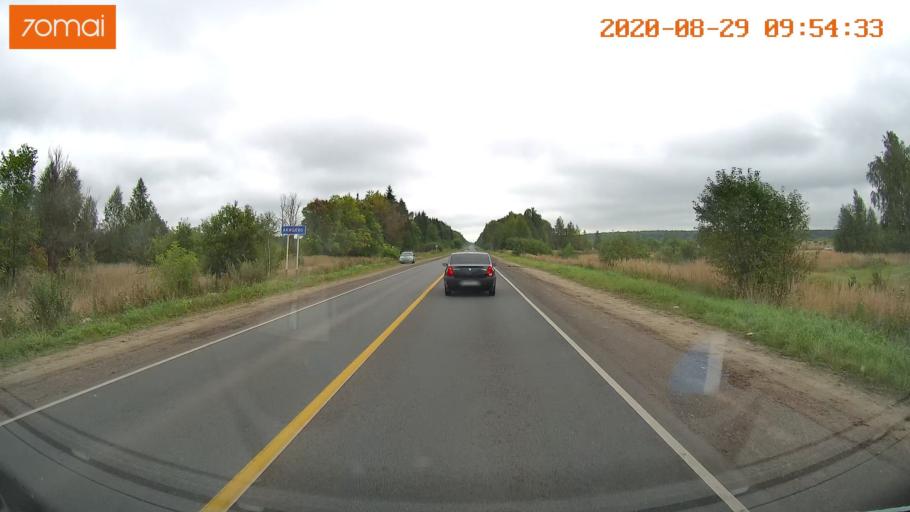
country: RU
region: Ivanovo
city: Zarechnyy
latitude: 57.4236
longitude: 42.2416
